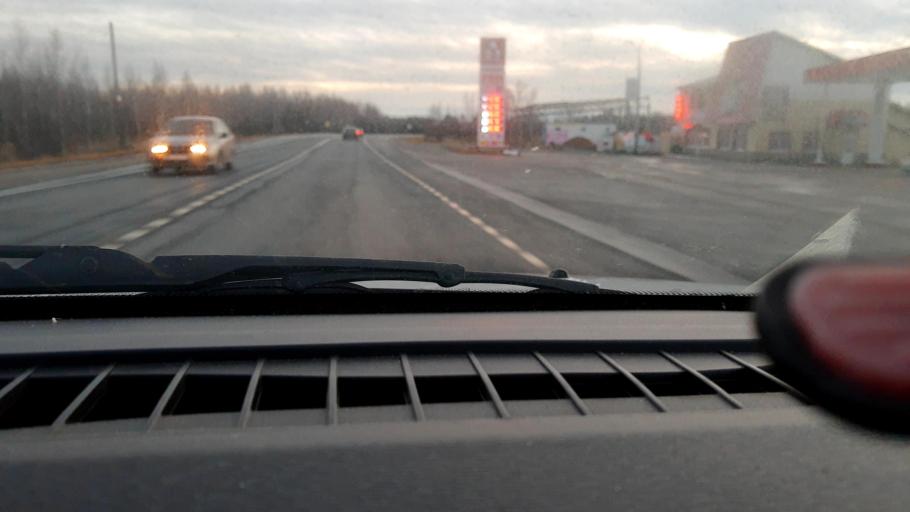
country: RU
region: Nizjnij Novgorod
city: Krasnyye Baki
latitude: 57.0869
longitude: 45.1476
